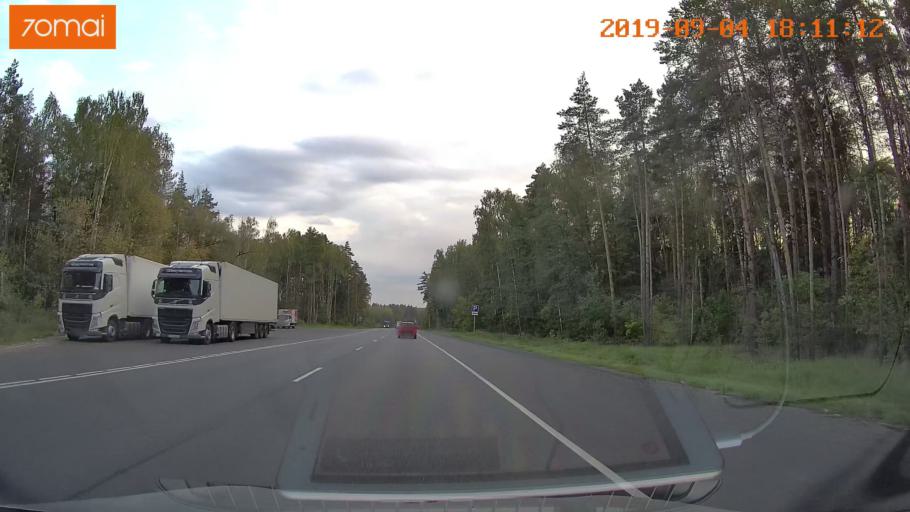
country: RU
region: Moskovskaya
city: Lopatinskiy
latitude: 55.3802
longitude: 38.7568
